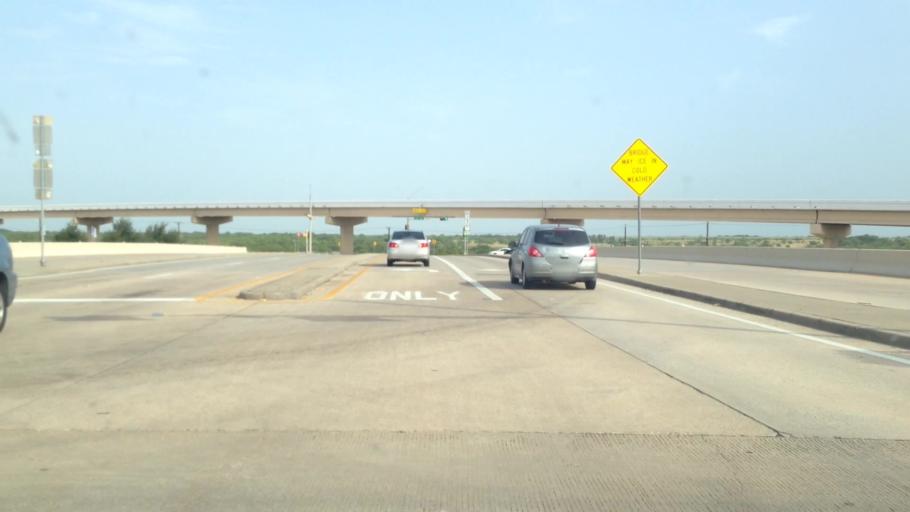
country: US
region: Texas
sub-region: Denton County
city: The Colony
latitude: 33.0505
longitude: -96.9192
